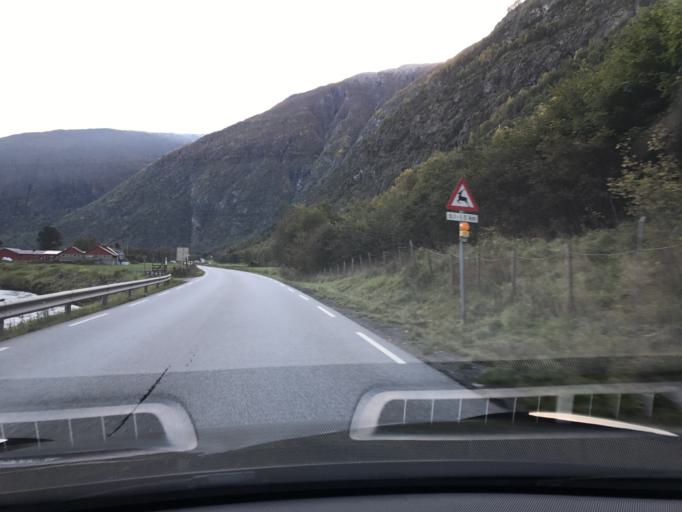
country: NO
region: Sogn og Fjordane
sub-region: Laerdal
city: Laerdalsoyri
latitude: 61.0887
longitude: 7.5135
